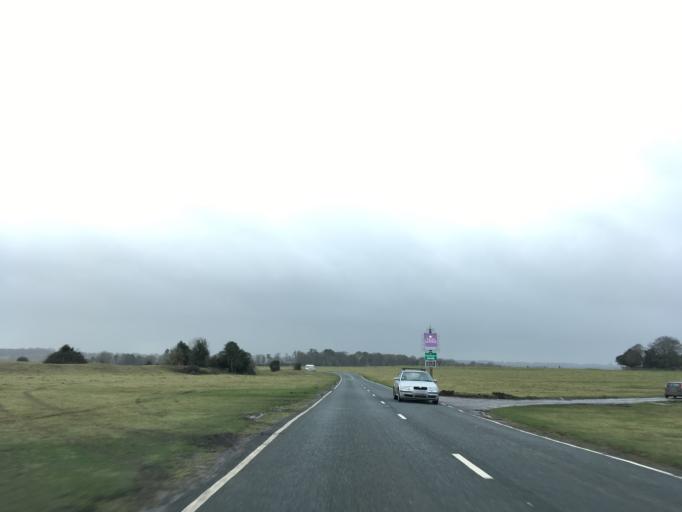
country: GB
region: England
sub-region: Gloucestershire
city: Nailsworth
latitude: 51.7078
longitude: -2.2076
